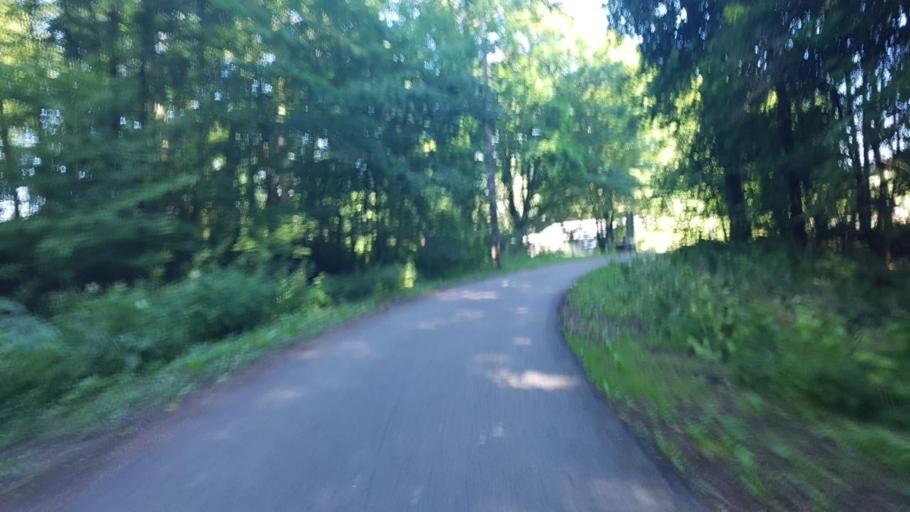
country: FR
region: Nord-Pas-de-Calais
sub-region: Departement du Nord
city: Anor
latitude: 49.9556
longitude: 4.1031
